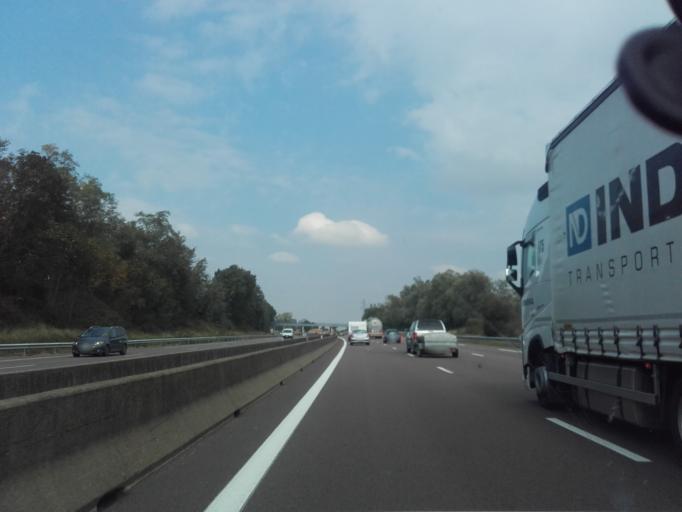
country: FR
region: Bourgogne
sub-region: Departement de Saone-et-Loire
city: Tournus
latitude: 46.5252
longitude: 4.9180
